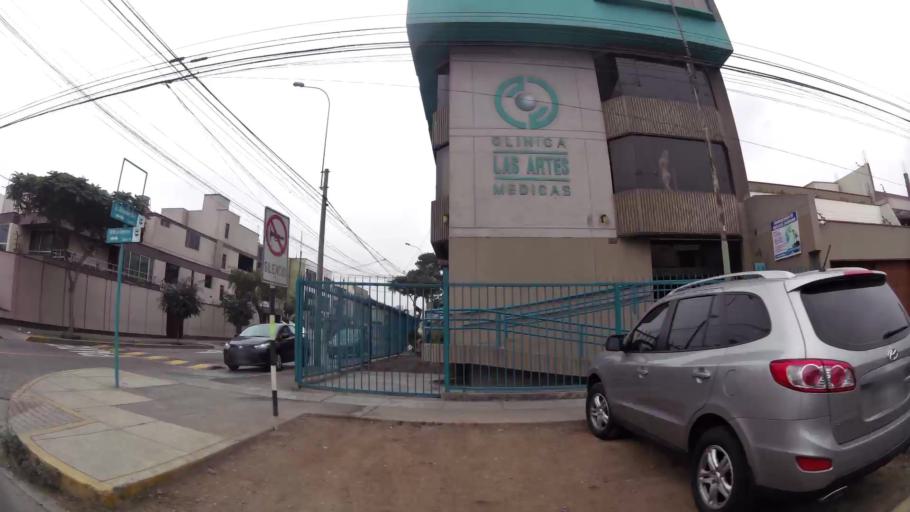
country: PE
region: Lima
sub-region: Lima
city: San Luis
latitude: -12.0897
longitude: -76.9954
